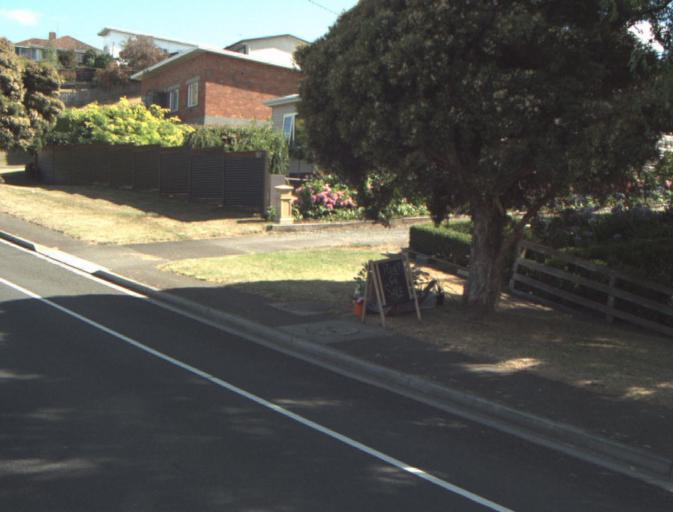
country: AU
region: Tasmania
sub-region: Launceston
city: Newstead
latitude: -41.4324
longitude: 147.1739
